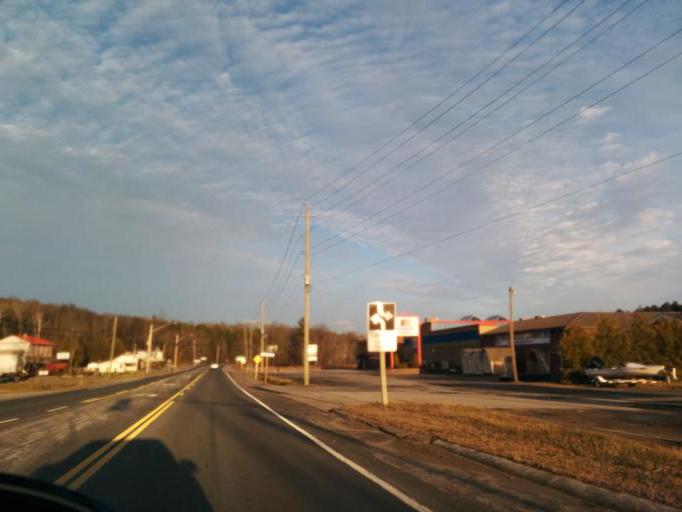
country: CA
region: Ontario
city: Bancroft
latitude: 45.0460
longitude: -78.5343
